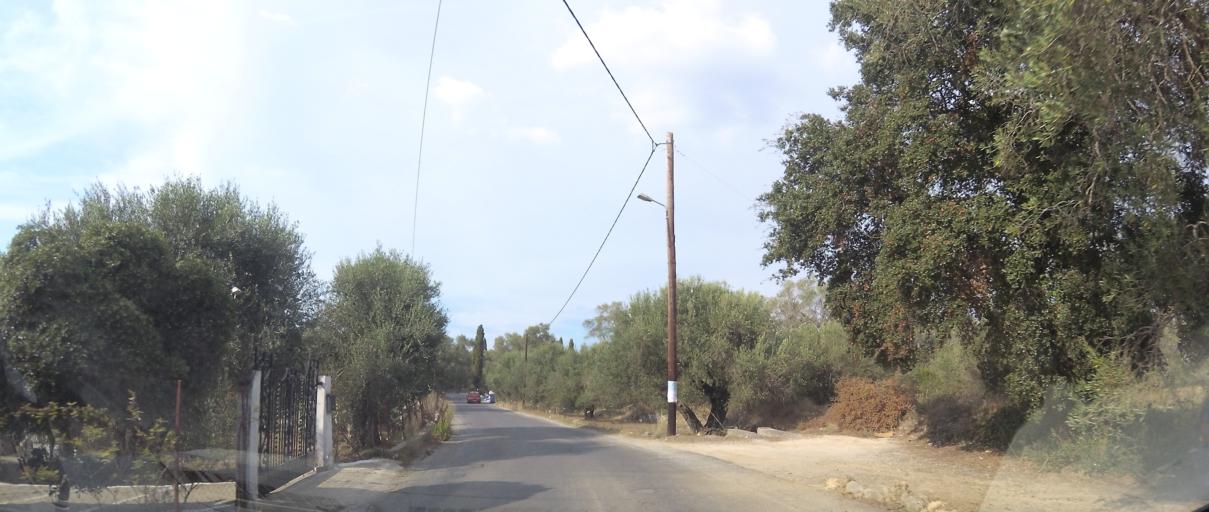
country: GR
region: Ionian Islands
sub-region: Nomos Kerkyras
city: Kynopiastes
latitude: 39.5574
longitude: 19.8619
